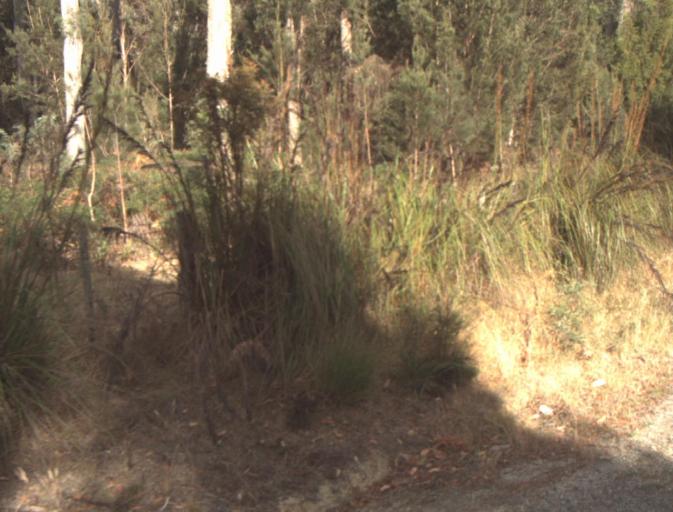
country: AU
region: Tasmania
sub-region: Dorset
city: Bridport
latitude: -41.1263
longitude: 147.2107
